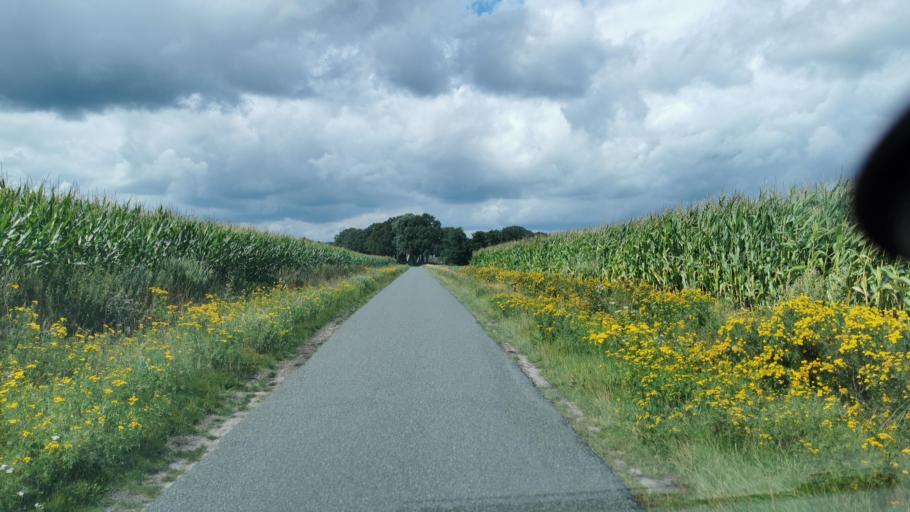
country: NL
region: Overijssel
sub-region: Gemeente Enschede
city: Enschede
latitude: 52.1457
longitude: 6.8420
